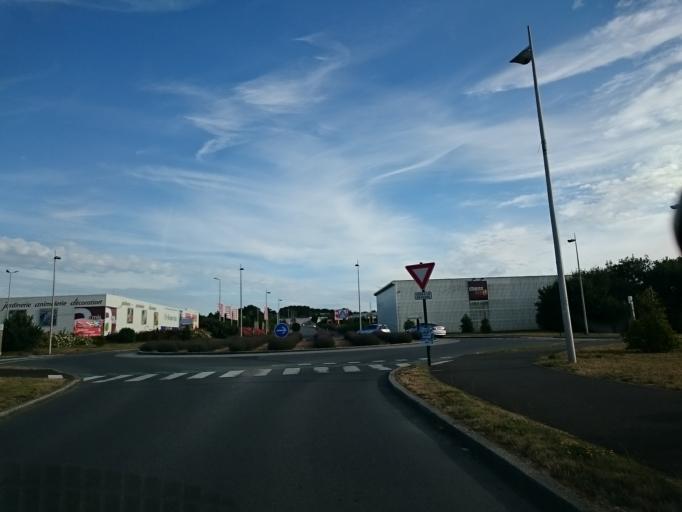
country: FR
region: Brittany
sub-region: Departement d'Ille-et-Vilaine
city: Bain-de-Bretagne
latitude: 47.8558
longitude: -1.6893
